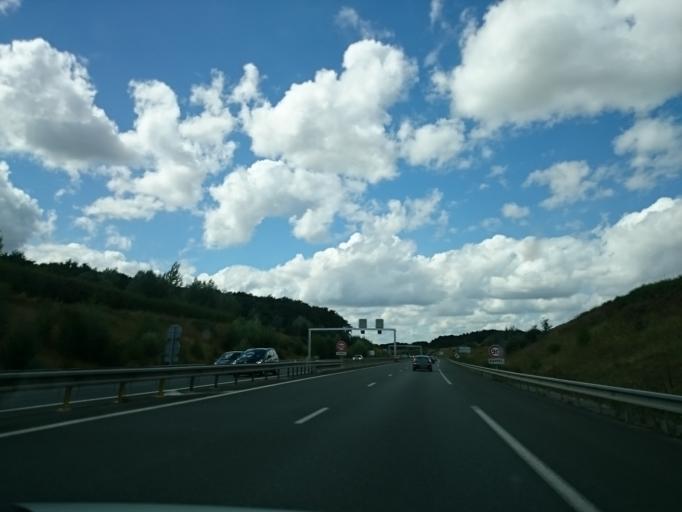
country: FR
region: Pays de la Loire
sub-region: Departement de Maine-et-Loire
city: Avrille
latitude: 47.4913
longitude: -0.5930
